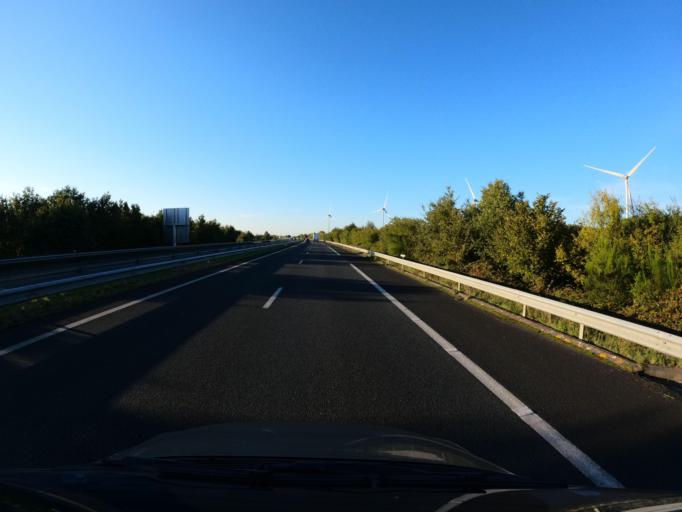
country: FR
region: Pays de la Loire
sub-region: Departement de la Vendee
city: Chauche
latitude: 46.8306
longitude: -1.2247
